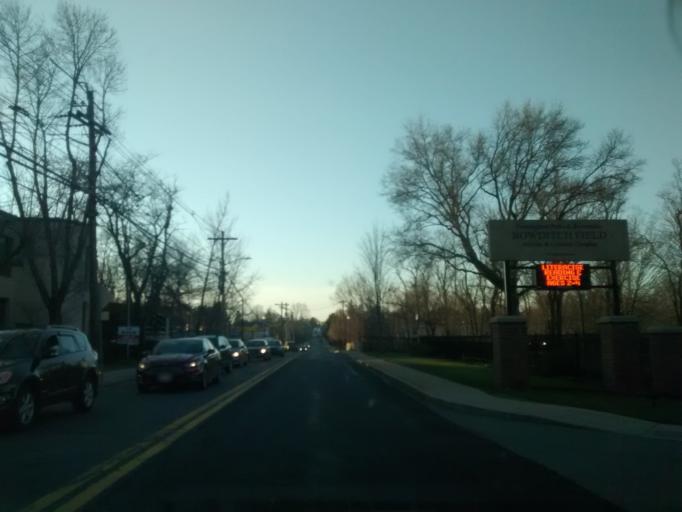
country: US
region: Massachusetts
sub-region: Middlesex County
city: Framingham Center
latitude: 42.2921
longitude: -71.4270
